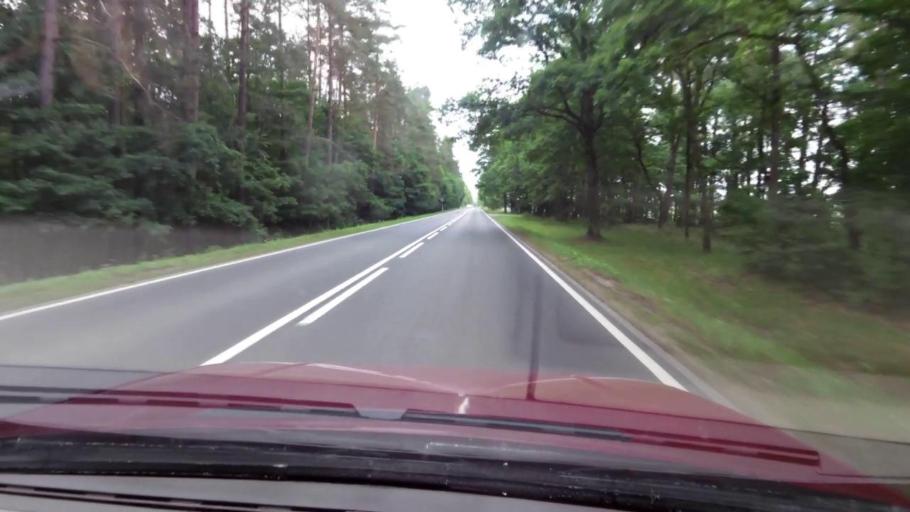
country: PL
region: Pomeranian Voivodeship
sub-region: Powiat bytowski
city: Trzebielino
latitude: 54.2558
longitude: 17.1042
